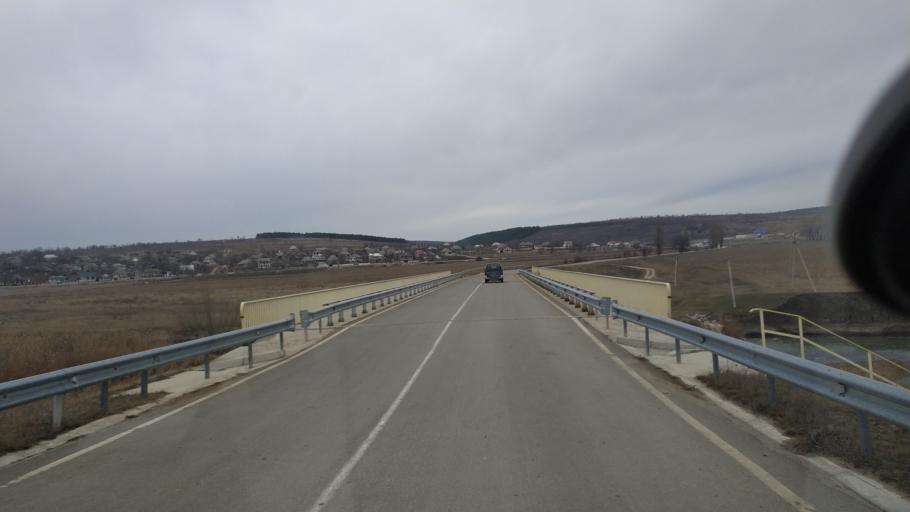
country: MD
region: Telenesti
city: Cocieri
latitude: 47.2615
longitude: 29.0541
